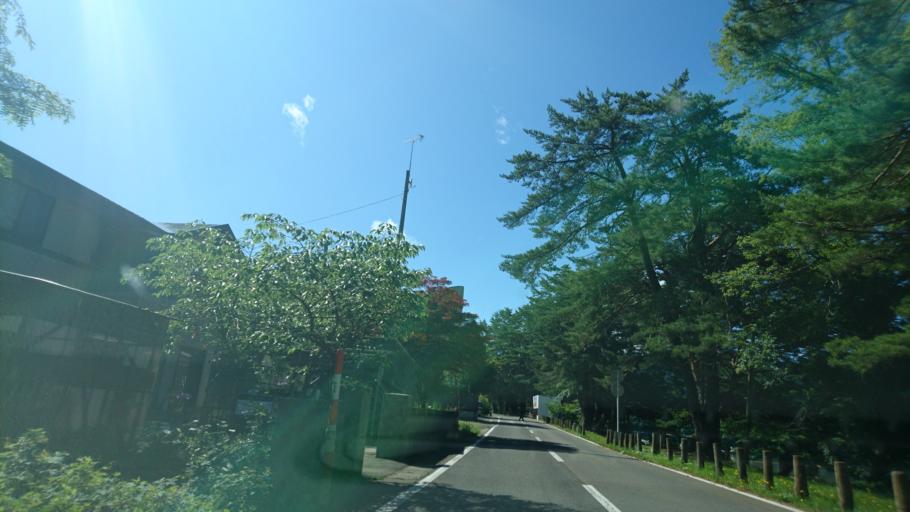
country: JP
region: Akita
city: Kakunodatemachi
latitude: 39.7351
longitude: 140.6970
